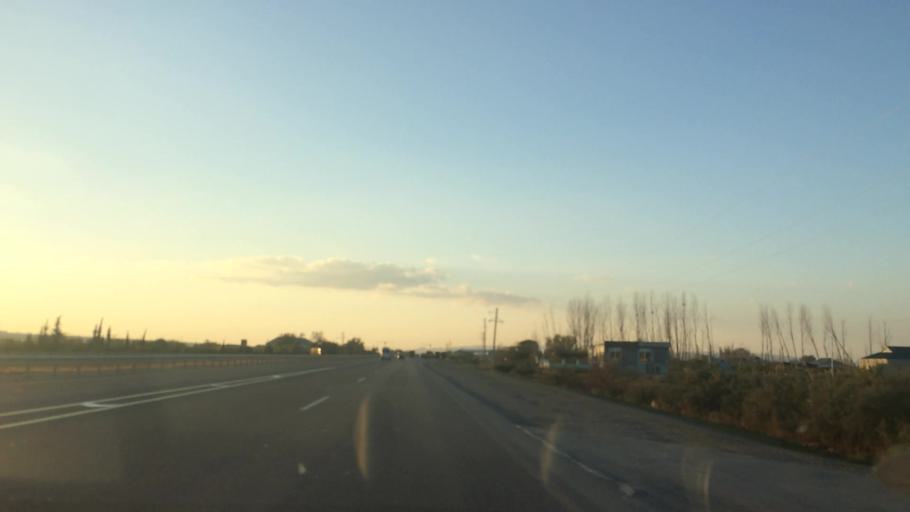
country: AZ
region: Haciqabul
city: Haciqabul
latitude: 40.0080
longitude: 49.1564
